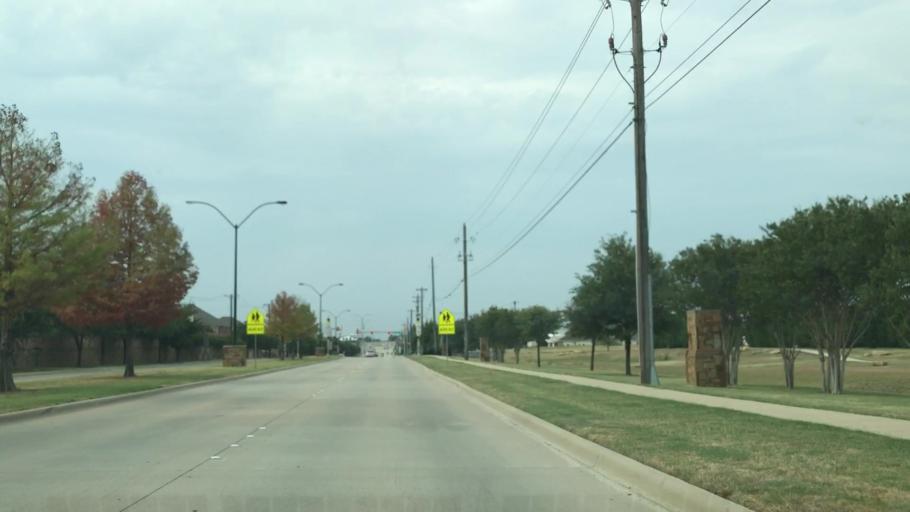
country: US
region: Texas
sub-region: Tarrant County
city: Keller
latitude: 32.9037
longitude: -97.2726
